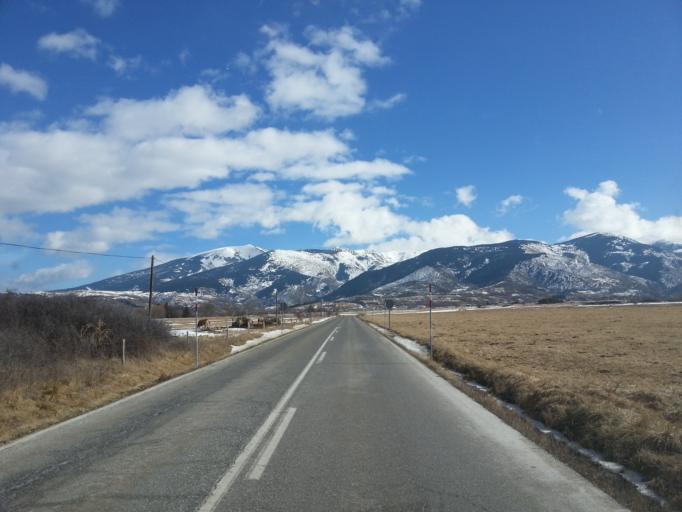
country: ES
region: Catalonia
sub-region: Provincia de Girona
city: Llivia
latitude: 42.4564
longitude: 2.0072
